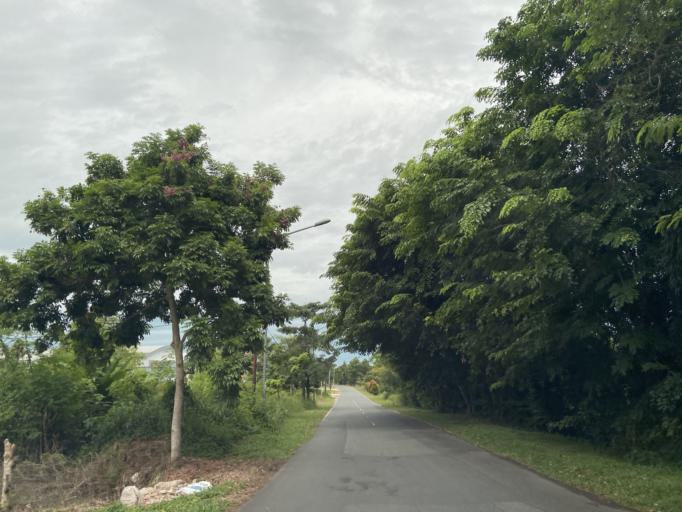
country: SG
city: Singapore
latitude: 1.1070
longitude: 104.0320
